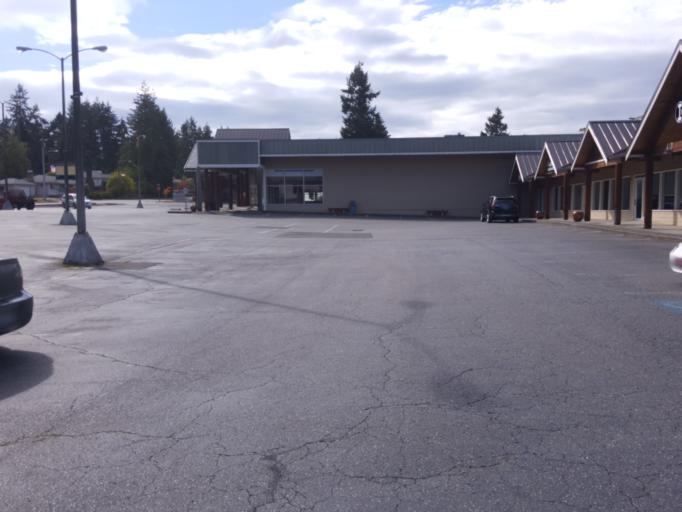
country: US
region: Washington
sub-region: Pierce County
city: Fircrest
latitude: 47.2393
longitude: -122.5182
